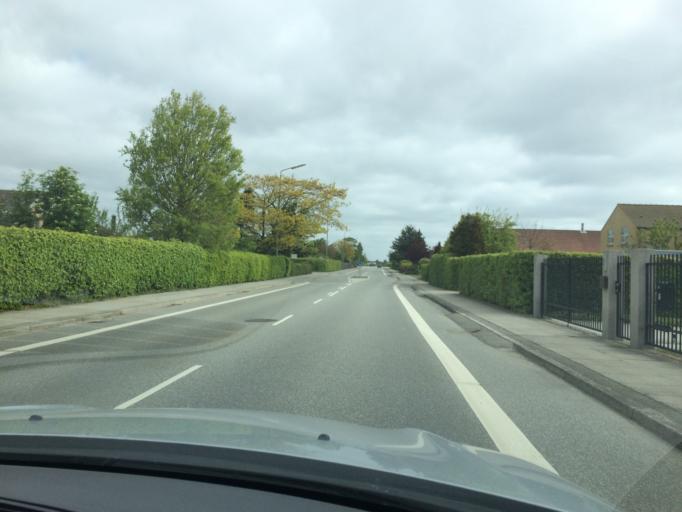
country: DK
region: Central Jutland
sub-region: Arhus Kommune
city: Hjortshoj
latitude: 56.2183
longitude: 10.2944
